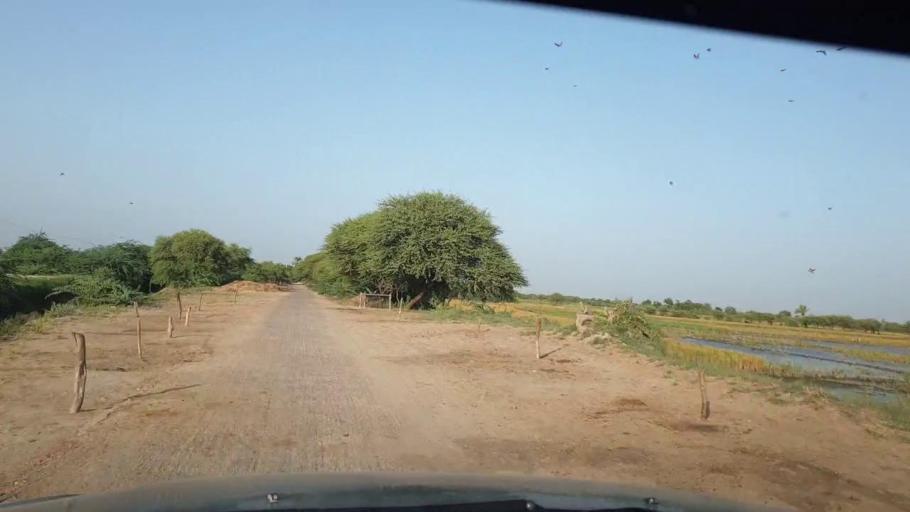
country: PK
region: Sindh
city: Rajo Khanani
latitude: 25.0160
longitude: 68.7623
